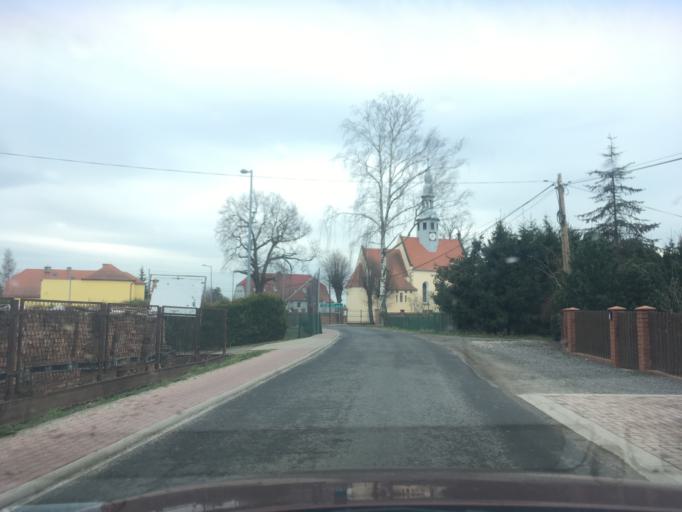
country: PL
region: Lower Silesian Voivodeship
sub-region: Powiat zgorzelecki
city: Lagow
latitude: 51.1589
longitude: 15.0419
